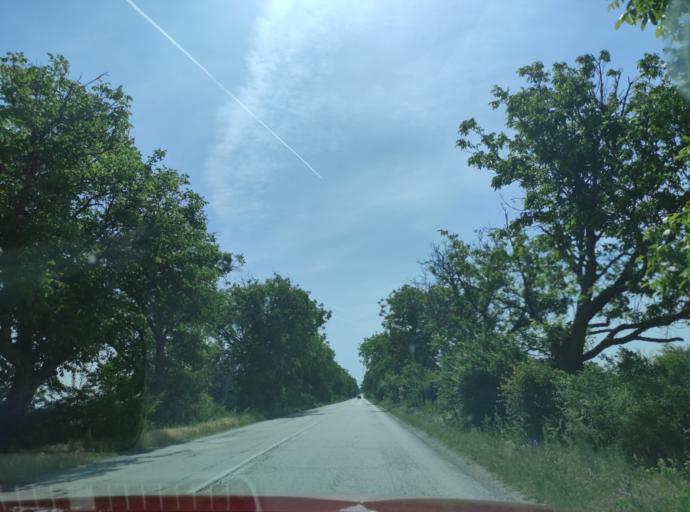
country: BG
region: Pleven
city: Iskur
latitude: 43.4471
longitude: 24.3277
